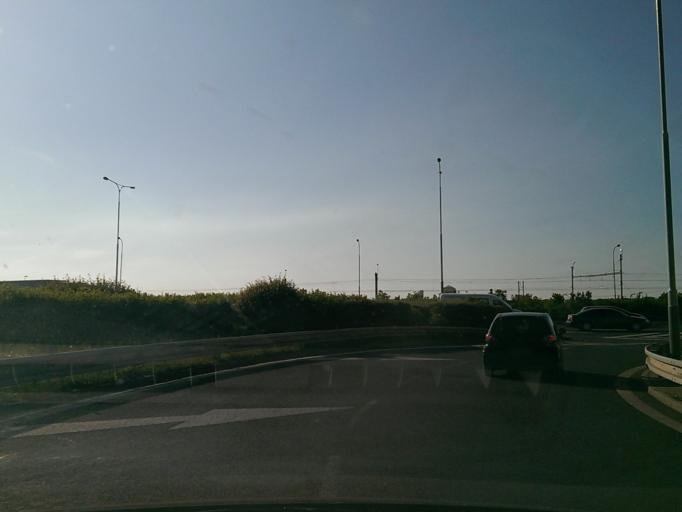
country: CZ
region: Praha
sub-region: Praha 8
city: Liben
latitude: 50.0600
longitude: 14.4934
